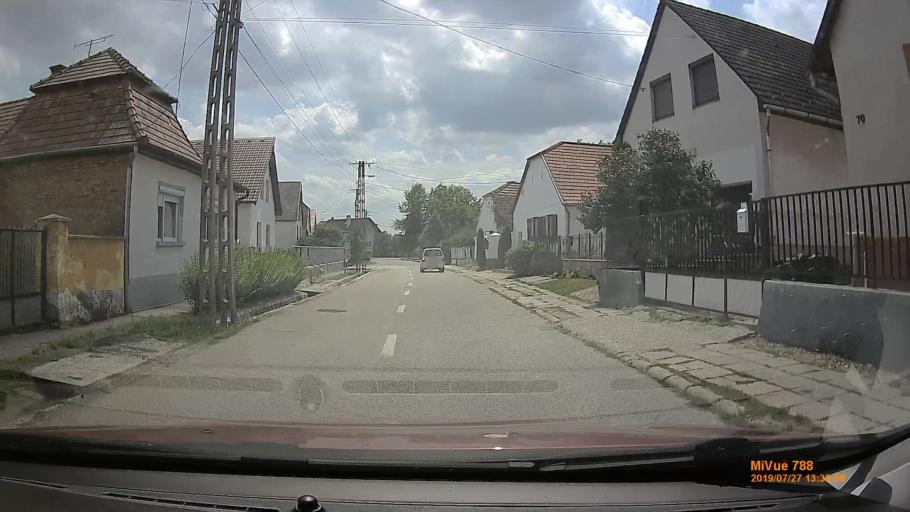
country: HU
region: Veszprem
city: Ajka
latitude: 47.1329
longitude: 17.5689
